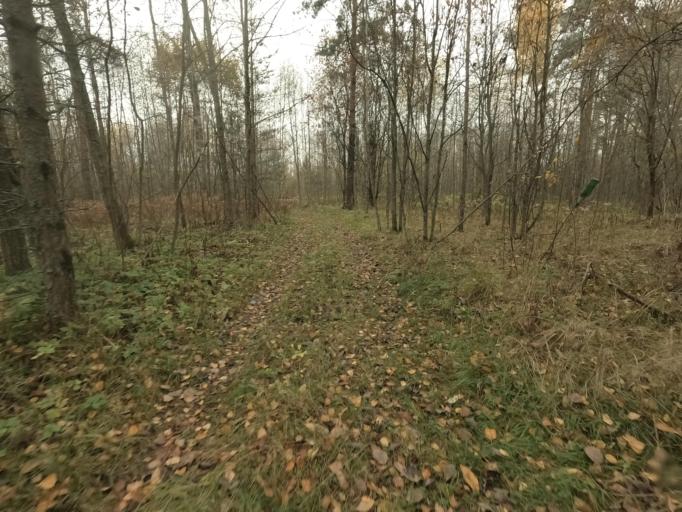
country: RU
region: Leningrad
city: Kirovsk
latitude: 59.8589
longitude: 30.9984
